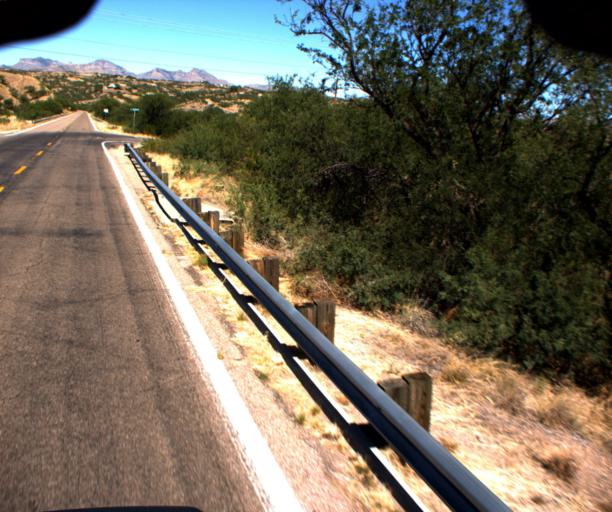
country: US
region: Arizona
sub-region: Santa Cruz County
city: Rio Rico
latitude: 31.4297
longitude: -110.9963
